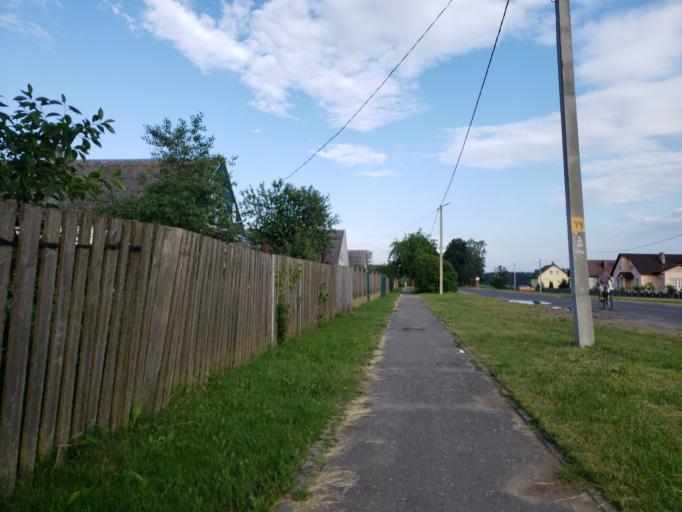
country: BY
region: Minsk
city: Chervyen'
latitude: 53.7015
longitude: 28.4439
